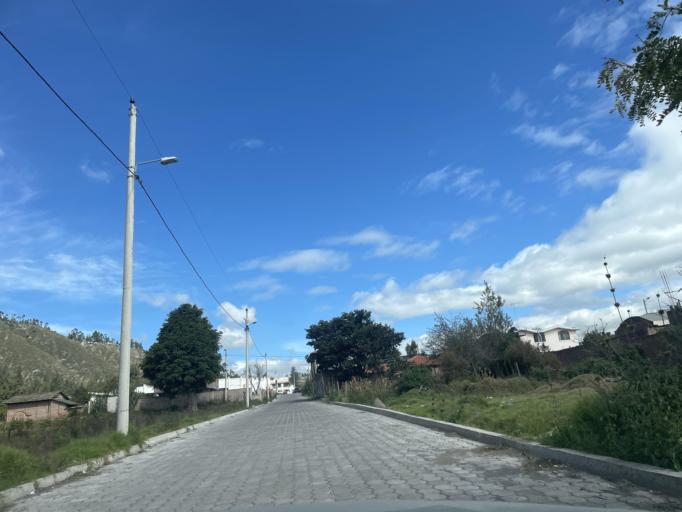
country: EC
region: Chimborazo
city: Guano
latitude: -1.6094
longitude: -78.6335
